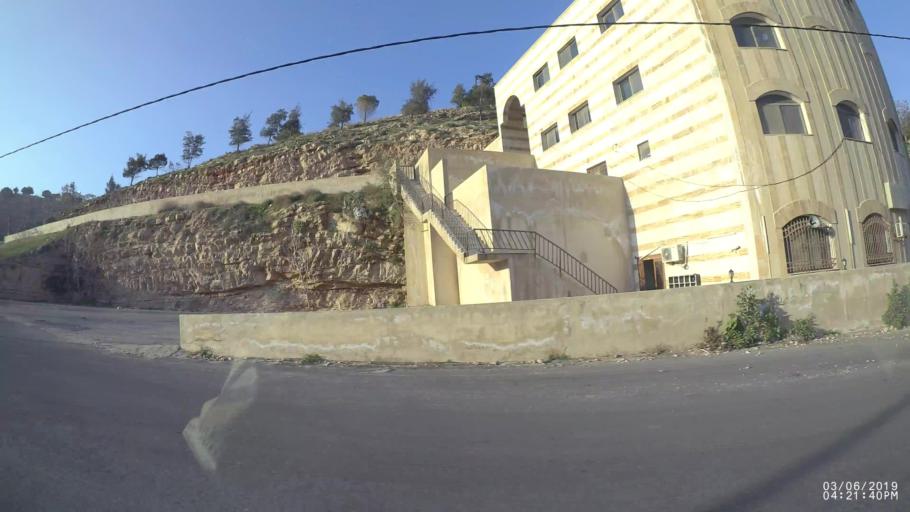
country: JO
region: Amman
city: Amman
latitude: 31.9816
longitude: 35.9645
